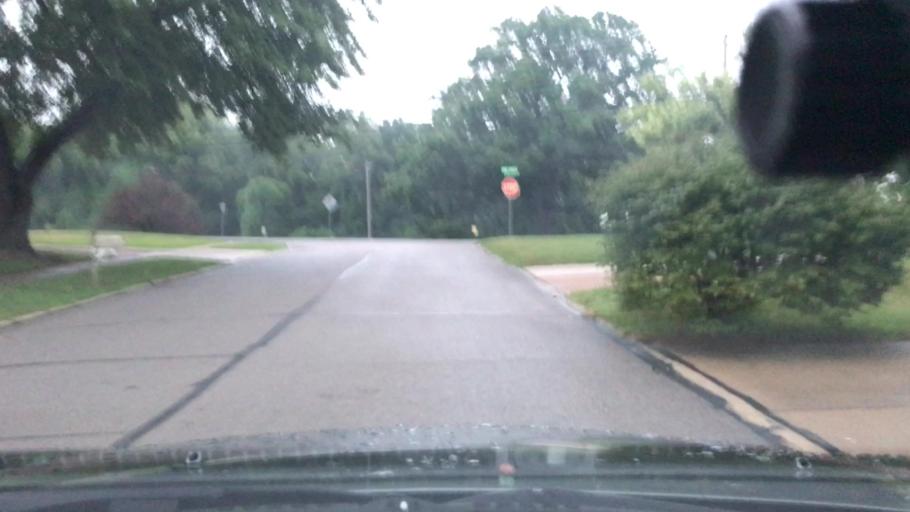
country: US
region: Missouri
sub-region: Saint Louis County
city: Maryland Heights
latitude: 38.6935
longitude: -90.4583
